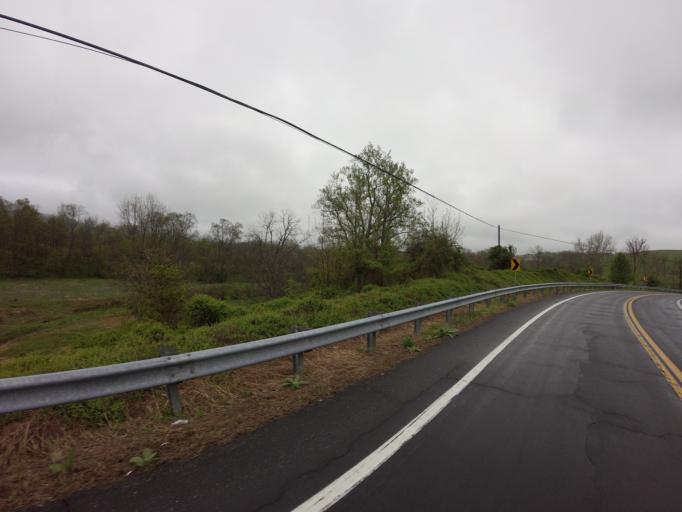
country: US
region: Maryland
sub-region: Frederick County
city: Myersville
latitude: 39.4839
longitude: -77.5336
